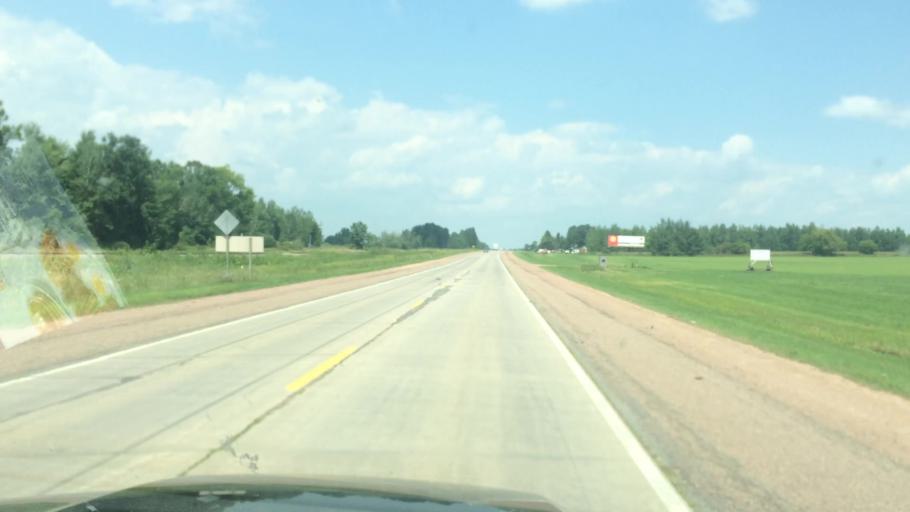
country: US
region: Wisconsin
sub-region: Clark County
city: Colby
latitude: 44.8751
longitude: -90.3157
